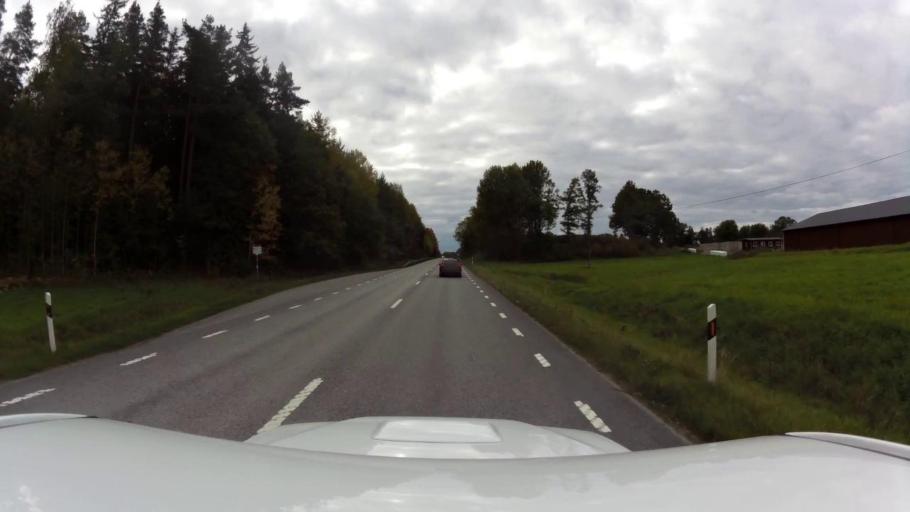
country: SE
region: OEstergoetland
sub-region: Kinda Kommun
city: Rimforsa
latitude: 58.1797
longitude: 15.6740
